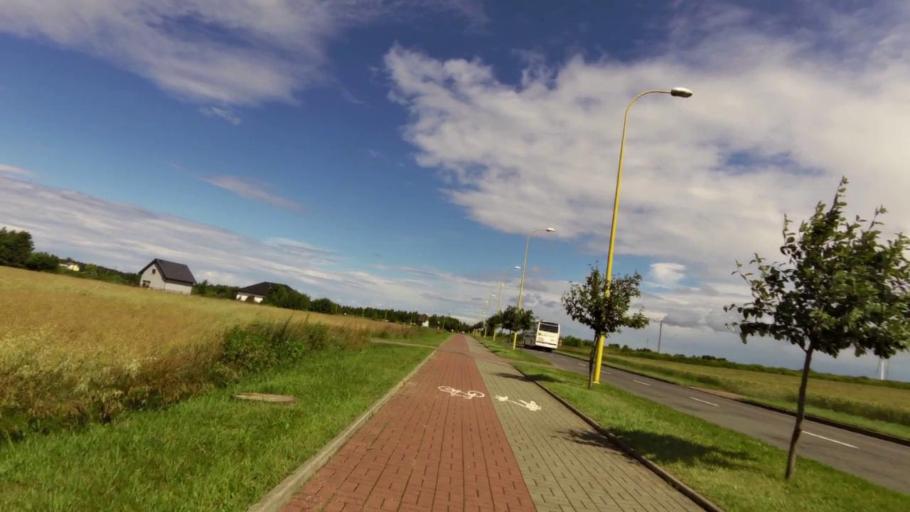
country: PL
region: West Pomeranian Voivodeship
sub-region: Powiat slawienski
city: Darlowo
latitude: 54.4398
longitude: 16.4075
